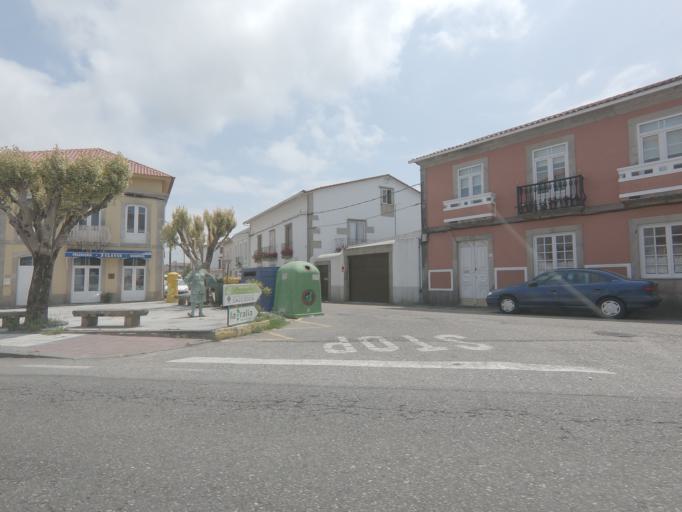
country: ES
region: Galicia
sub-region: Provincia de Pontevedra
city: A Guarda
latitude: 41.9065
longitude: -8.8622
